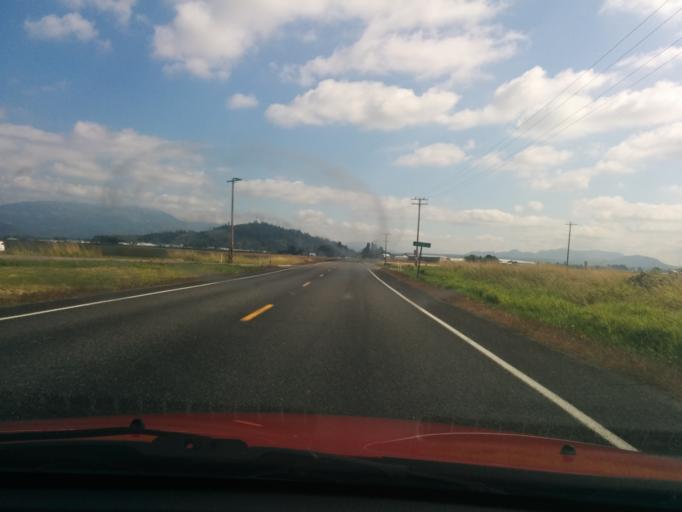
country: US
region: Washington
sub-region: Skagit County
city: Burlington
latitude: 48.5006
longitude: -122.3572
